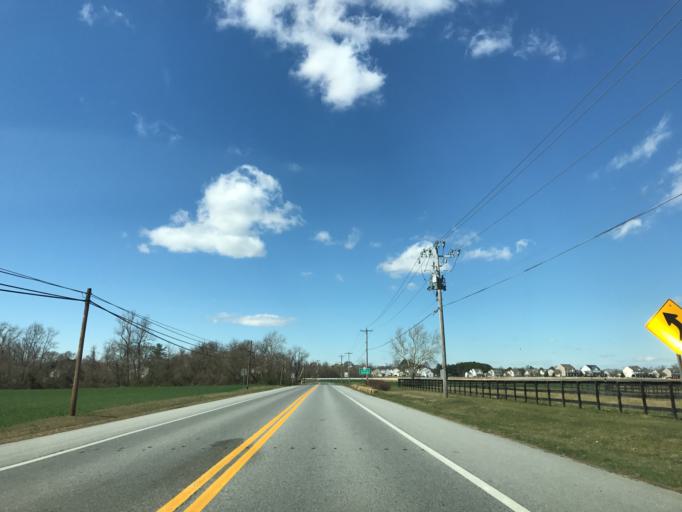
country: US
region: Maryland
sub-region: Queen Anne's County
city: Kingstown
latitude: 39.1368
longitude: -75.9783
